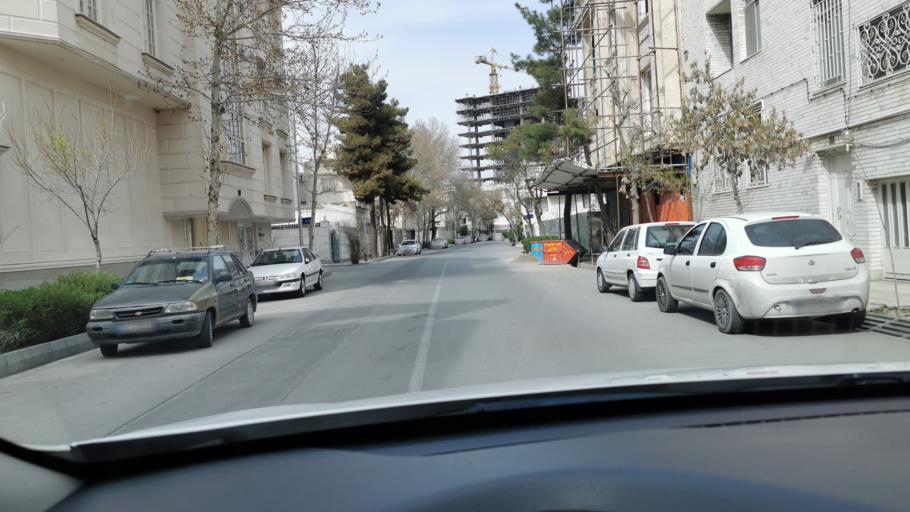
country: IR
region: Razavi Khorasan
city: Mashhad
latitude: 36.2929
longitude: 59.5747
